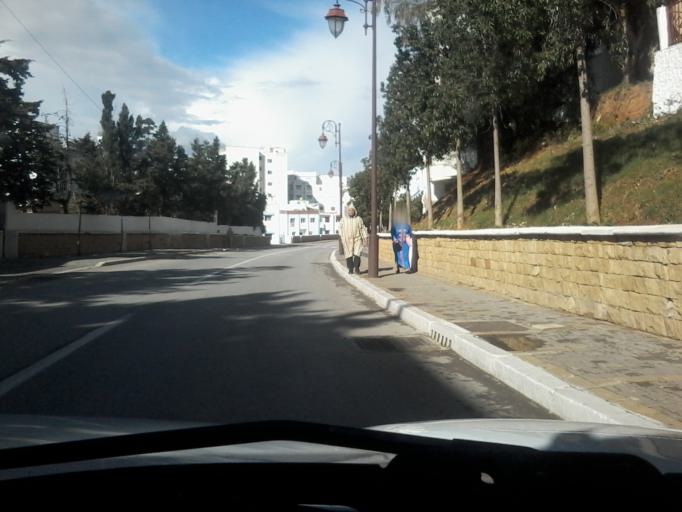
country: MA
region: Tanger-Tetouan
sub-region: Tetouan
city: Martil
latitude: 35.6858
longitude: -5.3306
